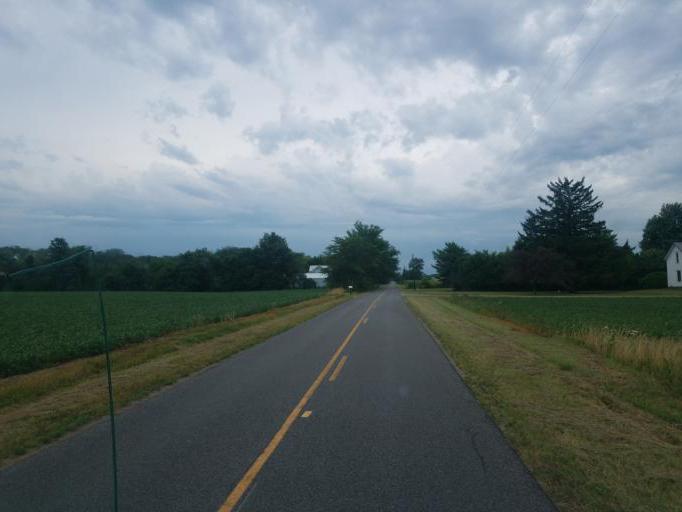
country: US
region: Ohio
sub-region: Paulding County
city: Antwerp
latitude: 41.2375
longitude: -84.7113
